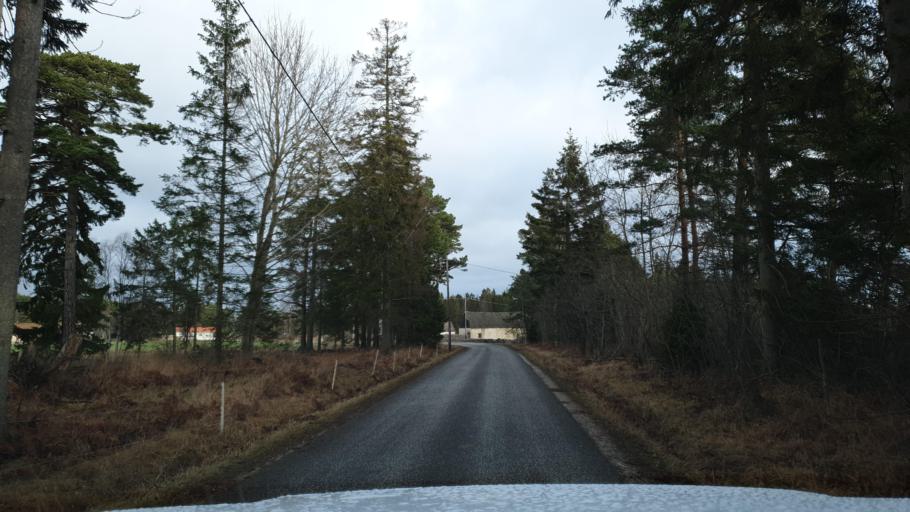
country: SE
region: Gotland
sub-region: Gotland
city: Slite
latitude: 57.3828
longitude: 18.8078
